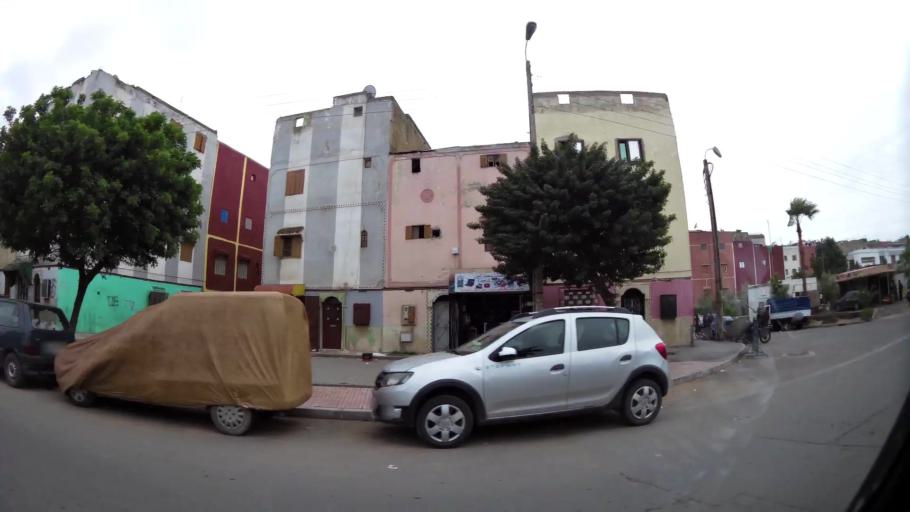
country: MA
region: Grand Casablanca
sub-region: Mediouna
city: Tit Mellil
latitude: 33.5636
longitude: -7.5403
